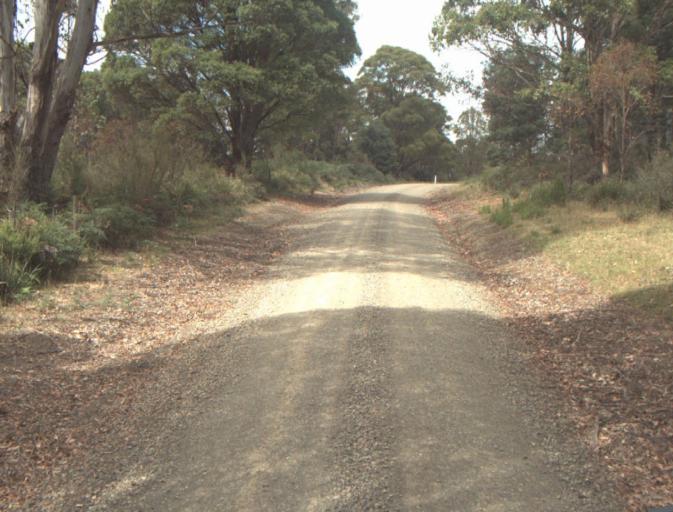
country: AU
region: Tasmania
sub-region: Northern Midlands
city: Evandale
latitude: -41.4513
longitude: 147.4775
